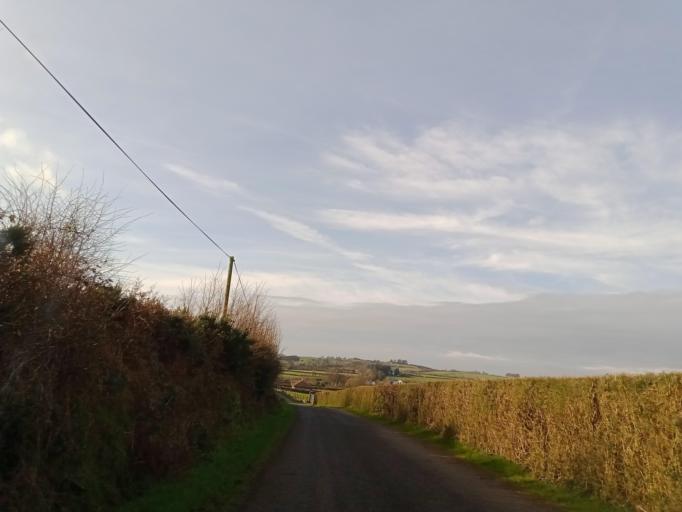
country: IE
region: Munster
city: Fethard
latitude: 52.5628
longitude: -7.6197
